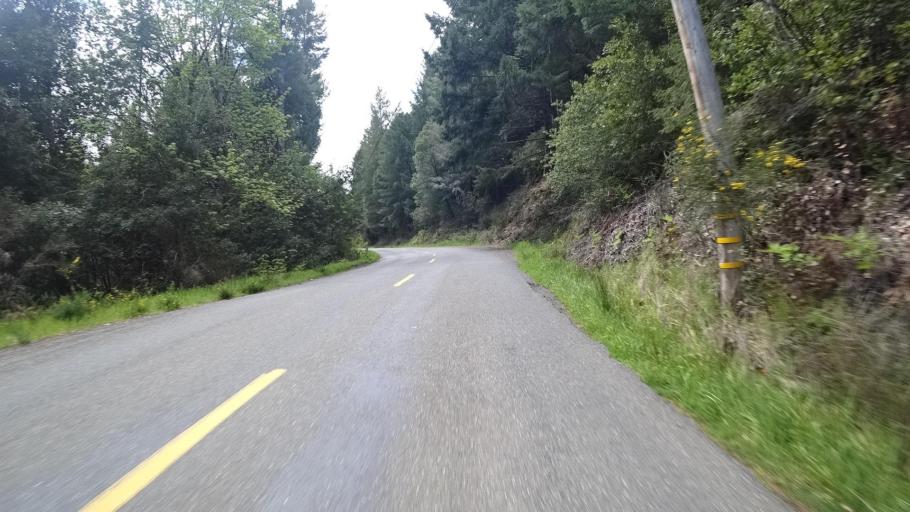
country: US
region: California
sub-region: Humboldt County
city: Redway
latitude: 40.0727
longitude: -123.9577
